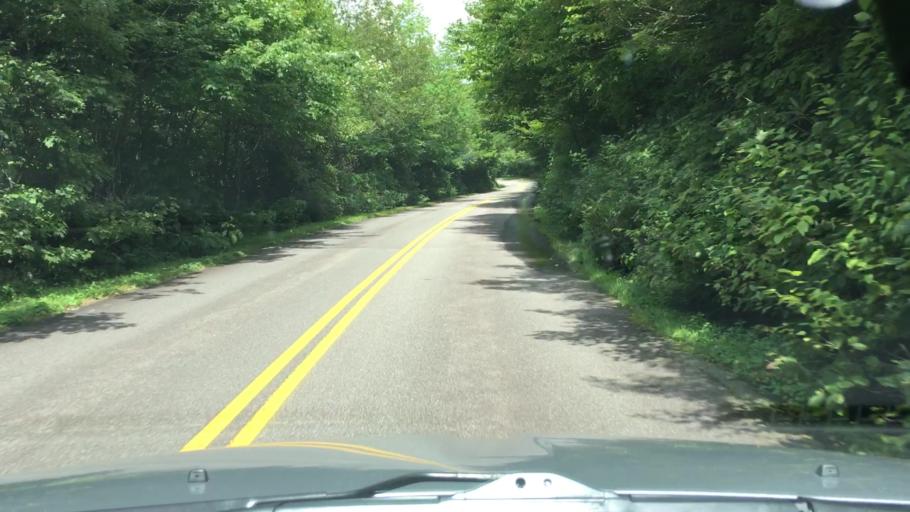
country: US
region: North Carolina
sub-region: Buncombe County
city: Black Mountain
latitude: 35.7036
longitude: -82.2551
